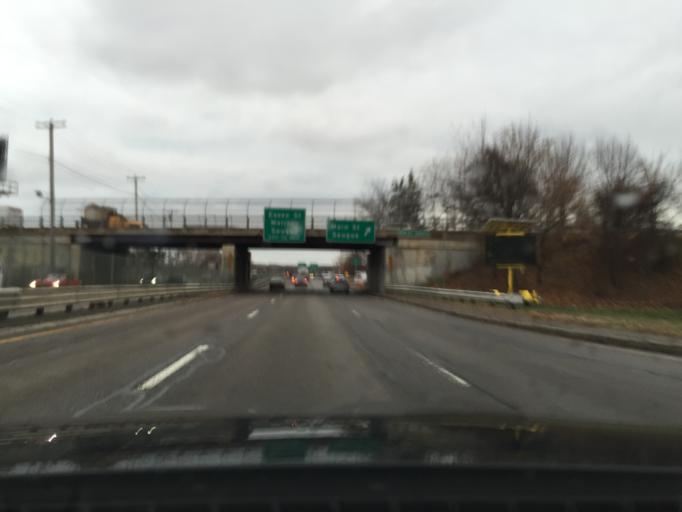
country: US
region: Massachusetts
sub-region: Essex County
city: Saugus
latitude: 42.4655
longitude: -71.0253
